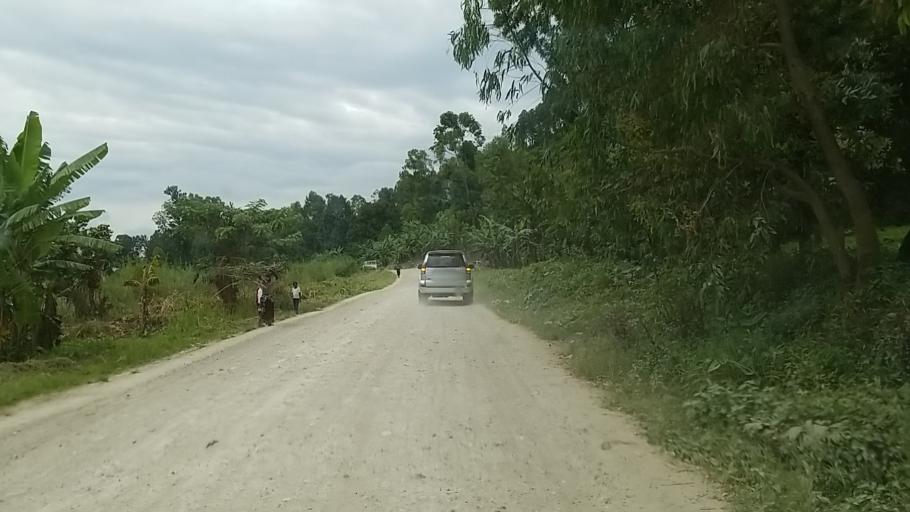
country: CD
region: Nord Kivu
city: Sake
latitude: -1.6012
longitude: 29.0371
